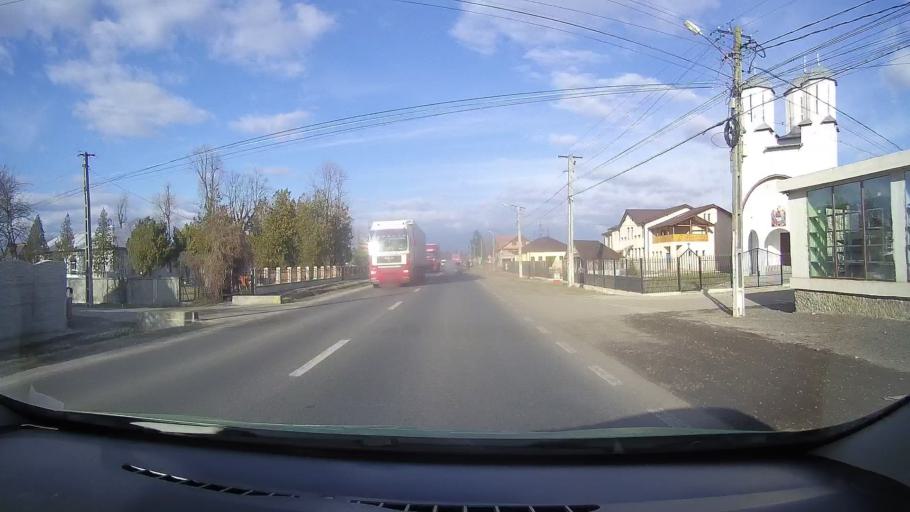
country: RO
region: Dambovita
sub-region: Comuna Ulmi
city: Viisoara
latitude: 44.8792
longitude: 25.4260
